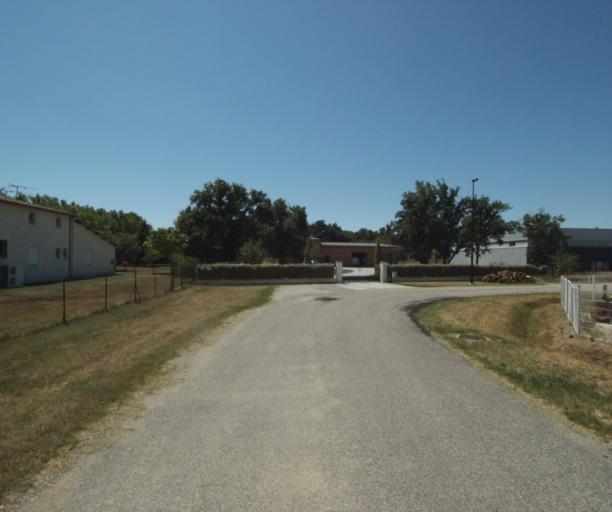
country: FR
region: Midi-Pyrenees
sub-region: Departement de la Haute-Garonne
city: Saint-Felix-Lauragais
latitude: 43.4446
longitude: 1.9436
